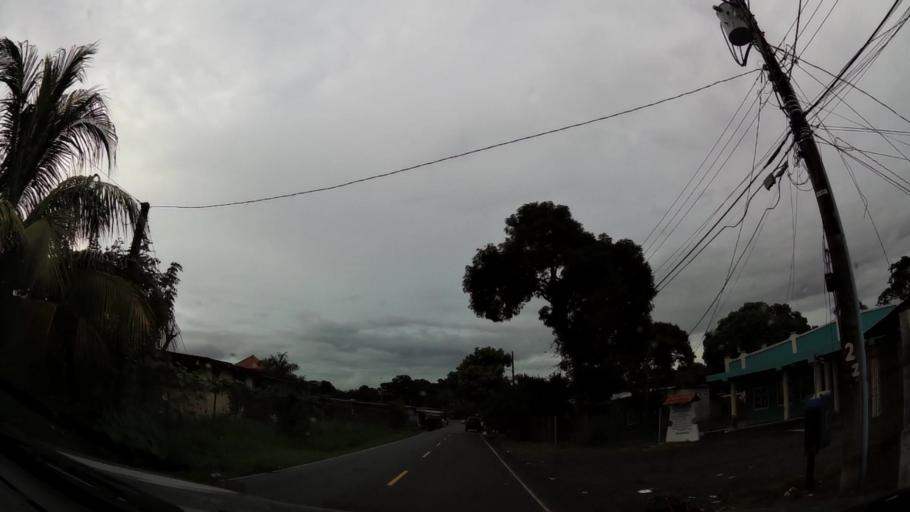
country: PA
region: Veraguas
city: Santiago de Veraguas
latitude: 8.0995
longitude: -80.9815
